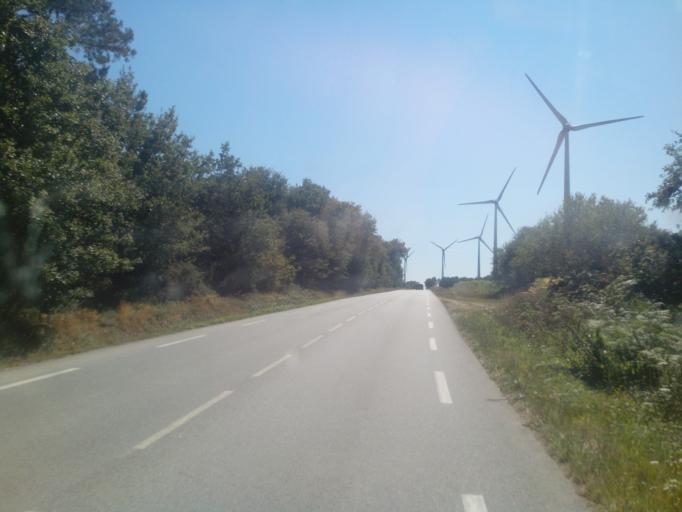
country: FR
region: Brittany
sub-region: Departement du Morbihan
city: Guillac
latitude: 47.8982
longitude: -2.5161
